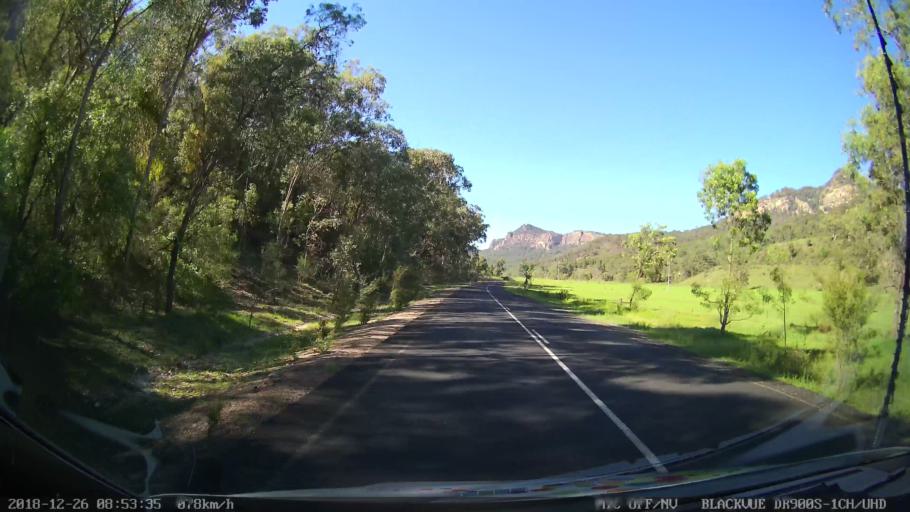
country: AU
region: New South Wales
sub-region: Mid-Western Regional
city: Kandos
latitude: -32.6057
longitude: 150.0769
